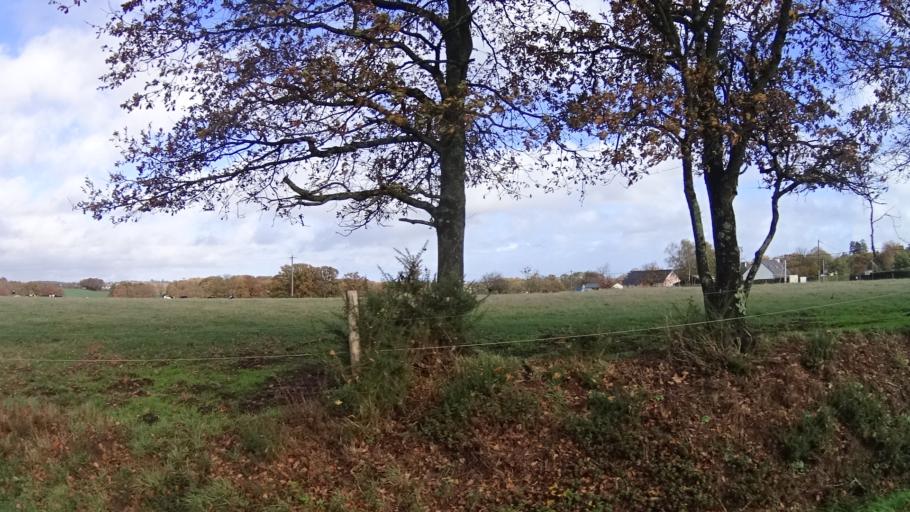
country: FR
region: Pays de la Loire
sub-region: Departement de la Loire-Atlantique
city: Saint-Nicolas-de-Redon
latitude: 47.6227
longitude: -2.0669
